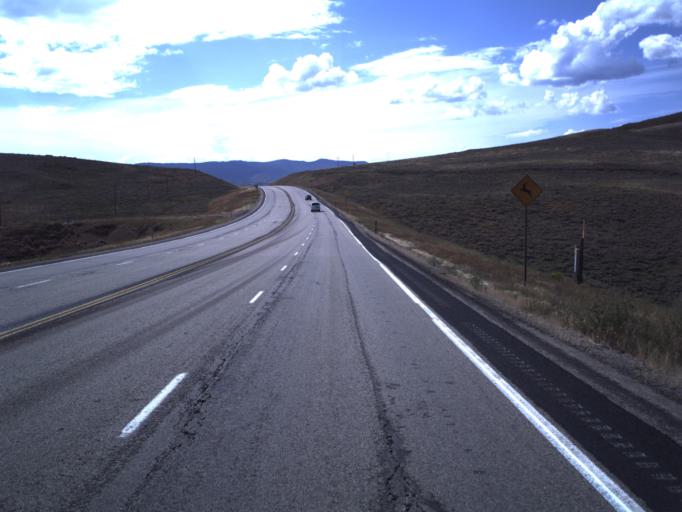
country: US
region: Utah
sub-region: Wasatch County
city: Heber
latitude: 40.1947
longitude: -111.0898
